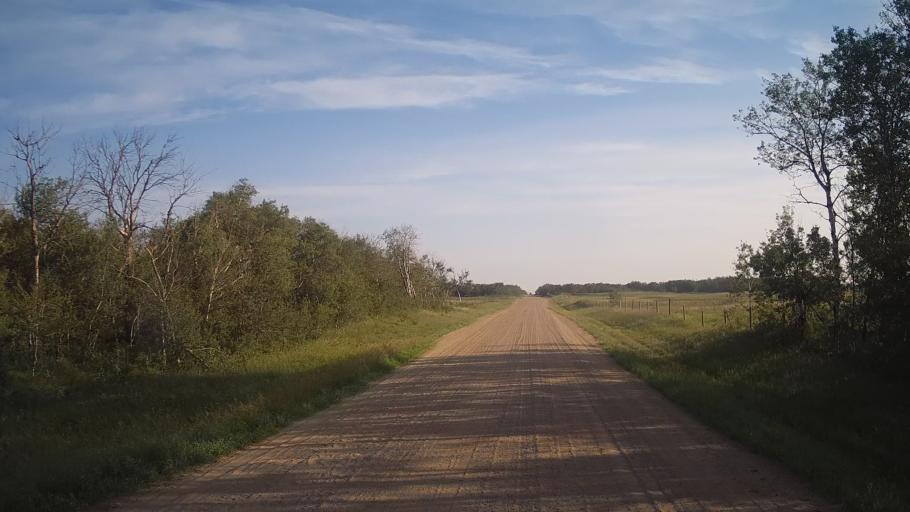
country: CA
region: Saskatchewan
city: Saskatoon
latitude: 51.8326
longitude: -106.5239
